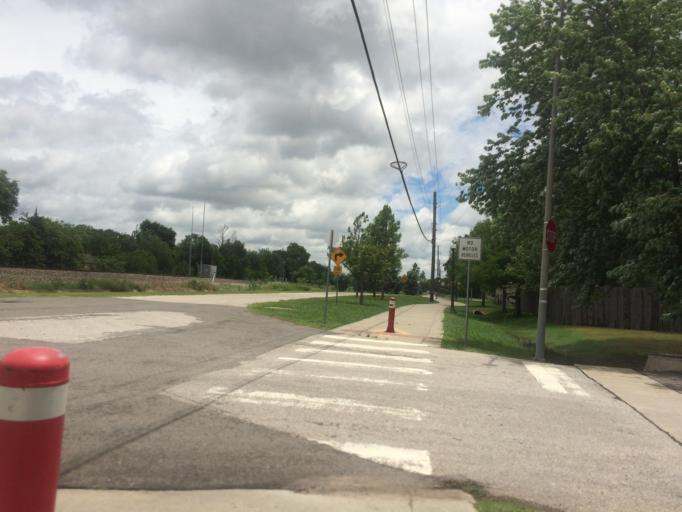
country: US
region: Oklahoma
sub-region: Cleveland County
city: Norman
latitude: 35.2313
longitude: -97.4507
